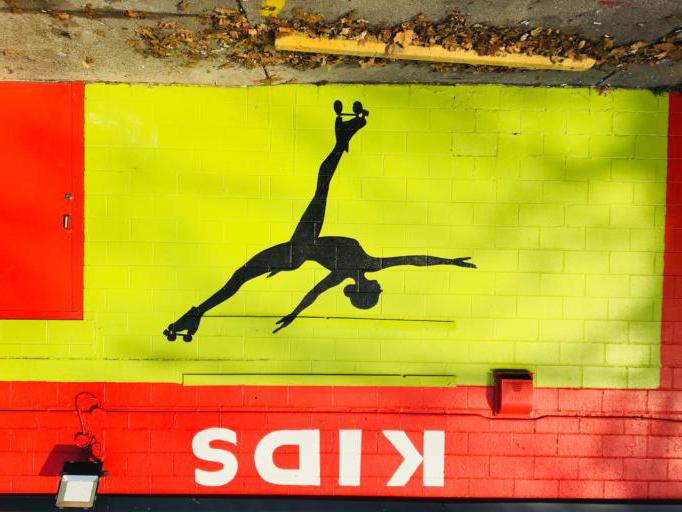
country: US
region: Michigan
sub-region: Wayne County
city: Dearborn
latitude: 42.3865
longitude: -83.2104
